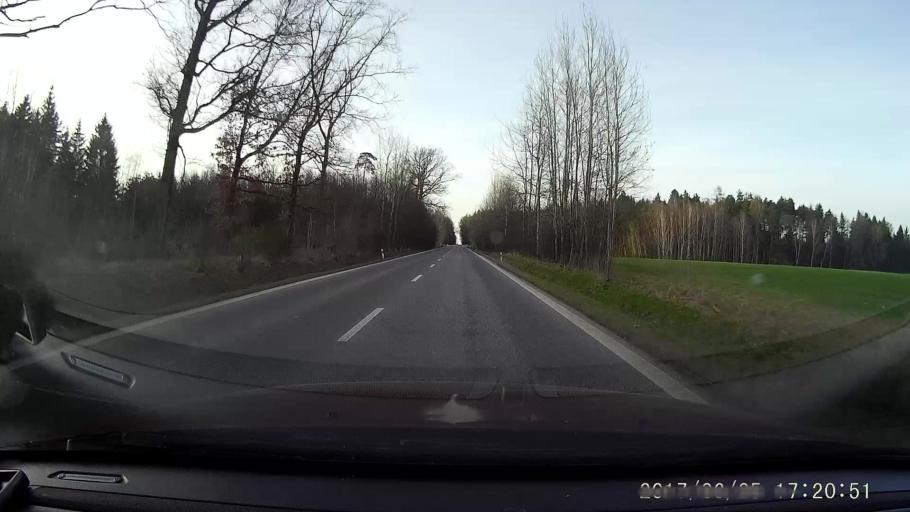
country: PL
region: Silesian Voivodeship
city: Zawidow
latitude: 50.9954
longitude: 15.0749
